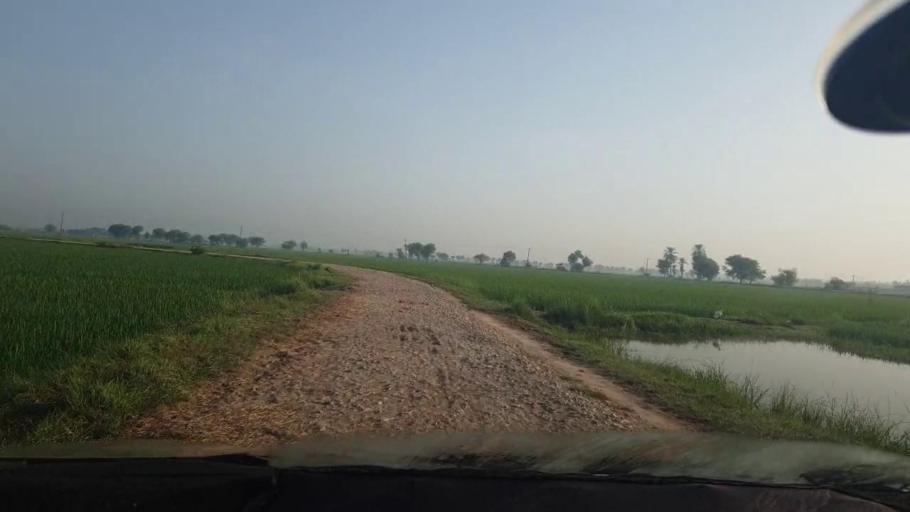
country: PK
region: Sindh
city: Kambar
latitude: 27.6272
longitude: 68.0185
